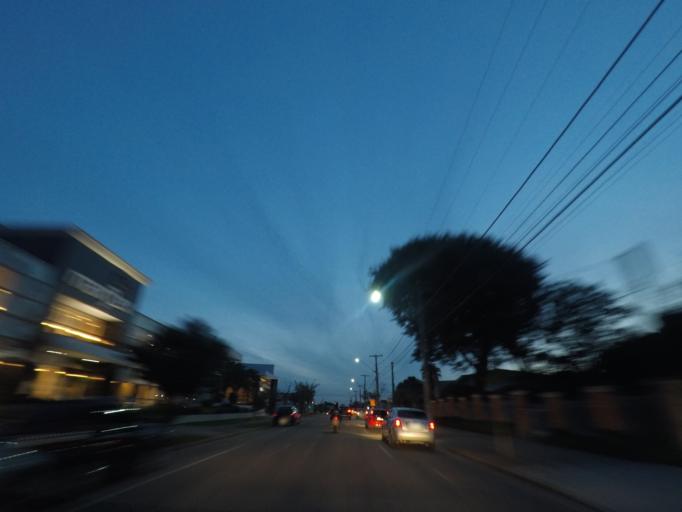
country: BR
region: Parana
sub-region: Curitiba
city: Curitiba
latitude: -25.4380
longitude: -49.2925
